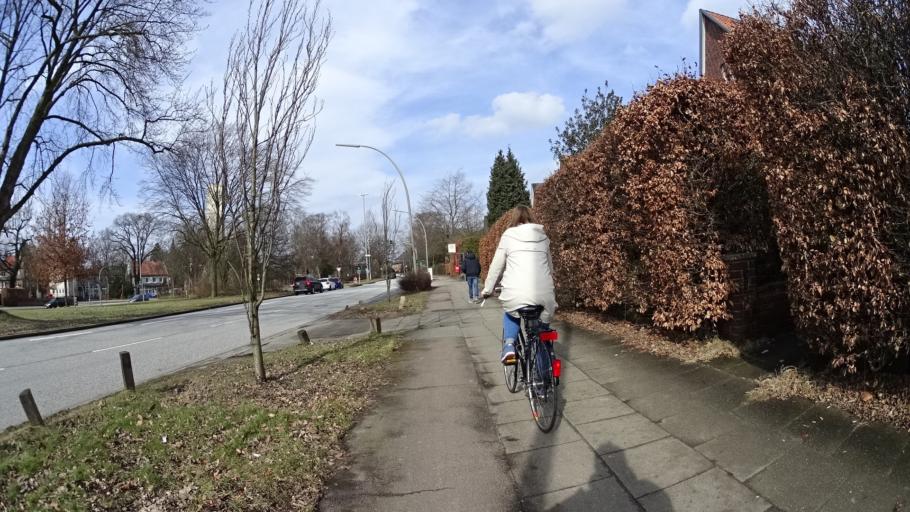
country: DE
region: Hamburg
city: Alsterdorf
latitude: 53.6084
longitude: 10.0123
